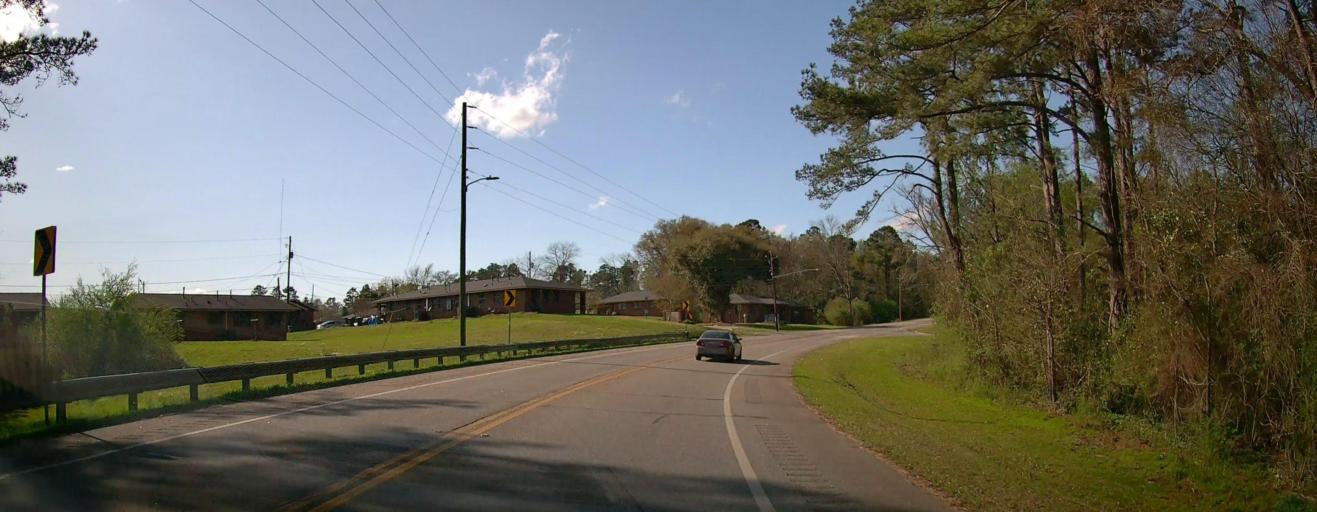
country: US
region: Georgia
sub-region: Baldwin County
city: Milledgeville
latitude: 33.0814
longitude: -83.2443
